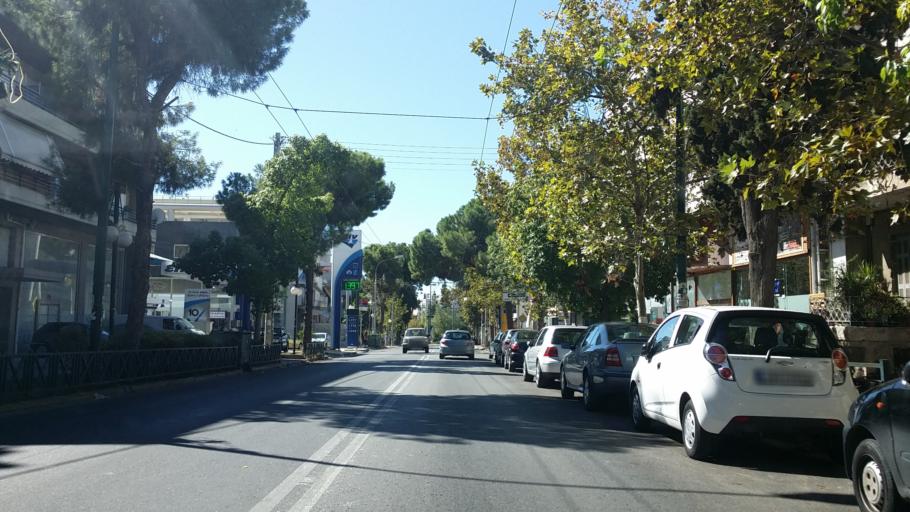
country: GR
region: Attica
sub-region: Nomarchia Athinas
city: Nea Chalkidona
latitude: 38.0286
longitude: 23.7336
